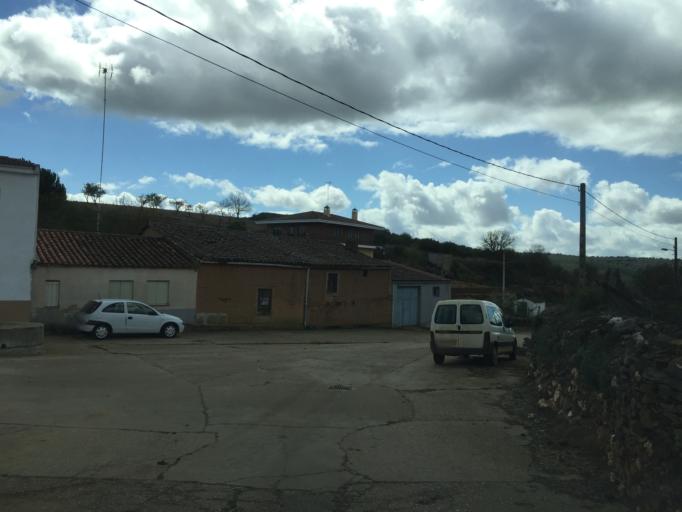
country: ES
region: Castille and Leon
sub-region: Provincia de Zamora
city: Manzanal del Barco
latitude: 41.5830
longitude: -5.9627
